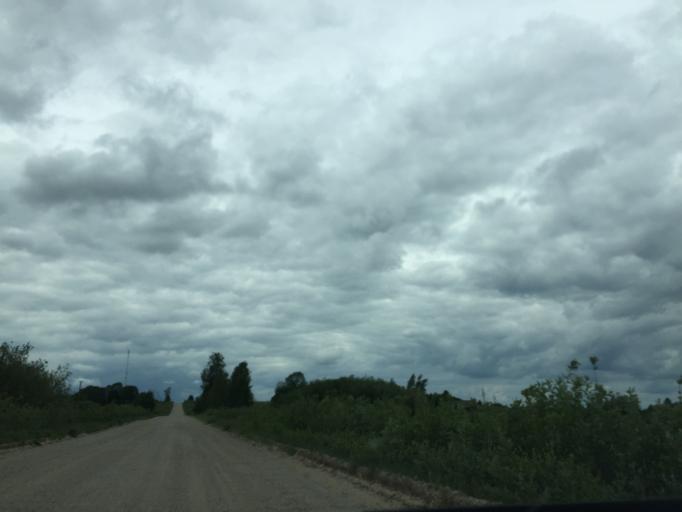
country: LV
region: Dagda
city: Dagda
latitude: 56.0094
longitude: 27.6031
